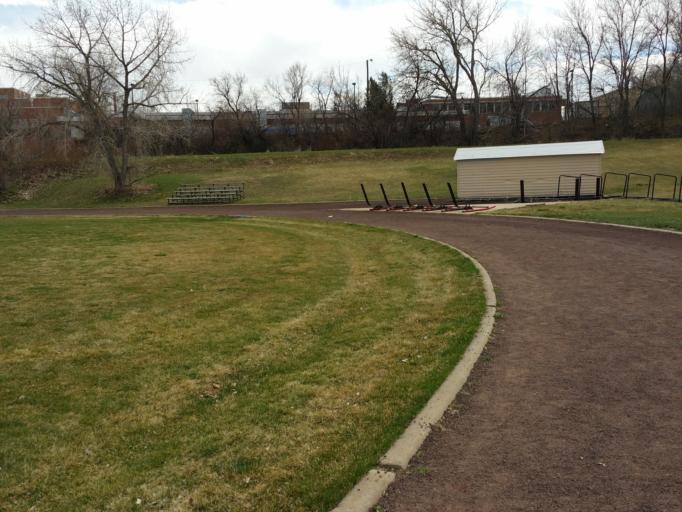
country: US
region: Colorado
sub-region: Jefferson County
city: Wheat Ridge
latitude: 39.7654
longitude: -105.1048
